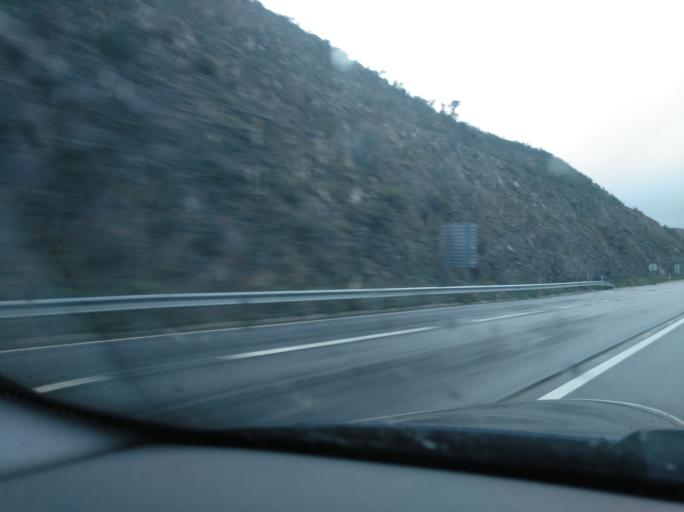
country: PT
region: Faro
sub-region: Alcoutim
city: Alcoutim
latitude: 37.3951
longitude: -7.5268
